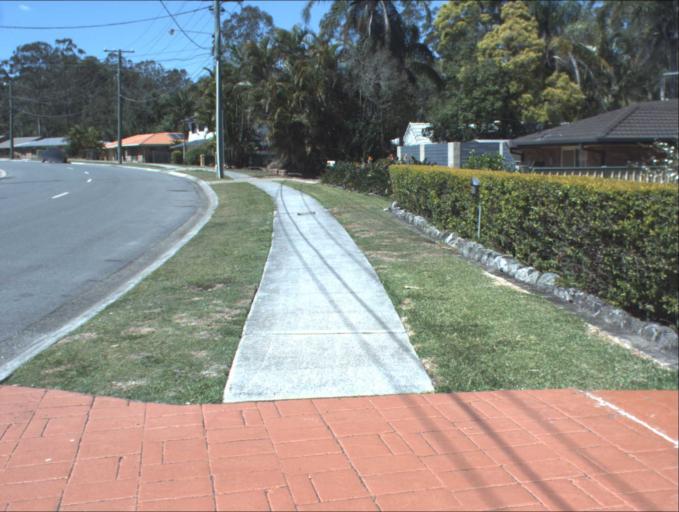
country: AU
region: Queensland
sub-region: Logan
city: Springwood
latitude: -27.6048
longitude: 153.1385
